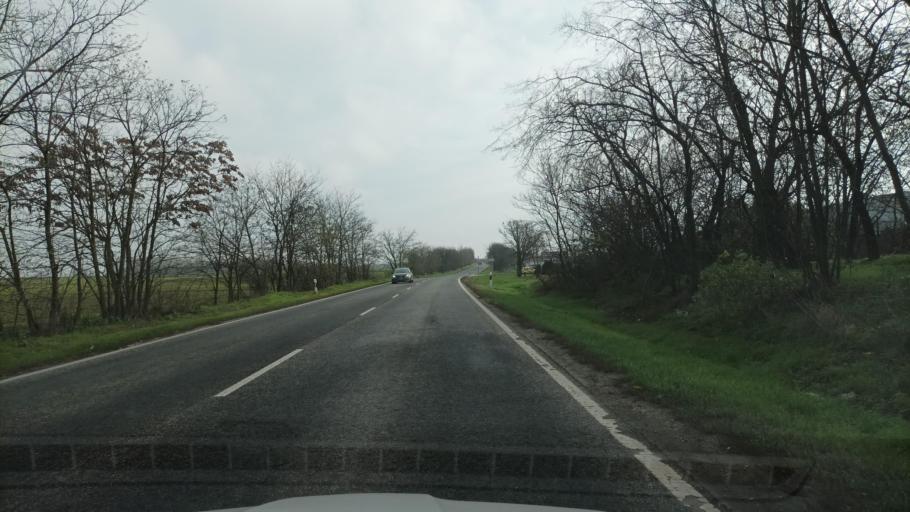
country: HU
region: Pest
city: Alsonemedi
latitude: 47.3540
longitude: 19.1606
